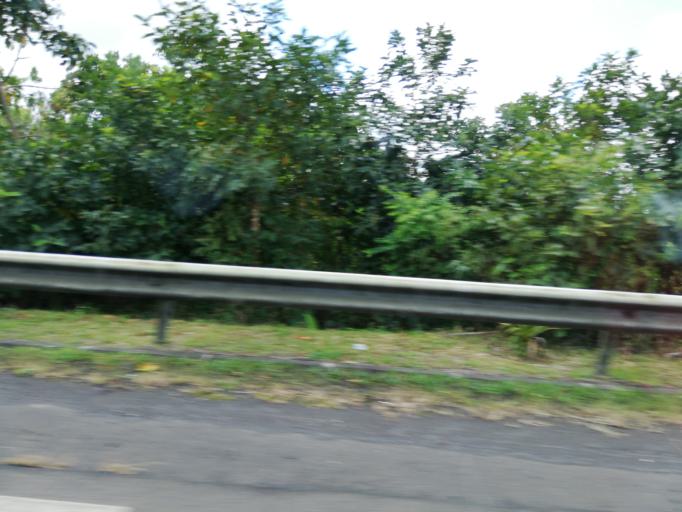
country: MU
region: Plaines Wilhems
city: Midlands
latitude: -20.3502
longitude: 57.5712
